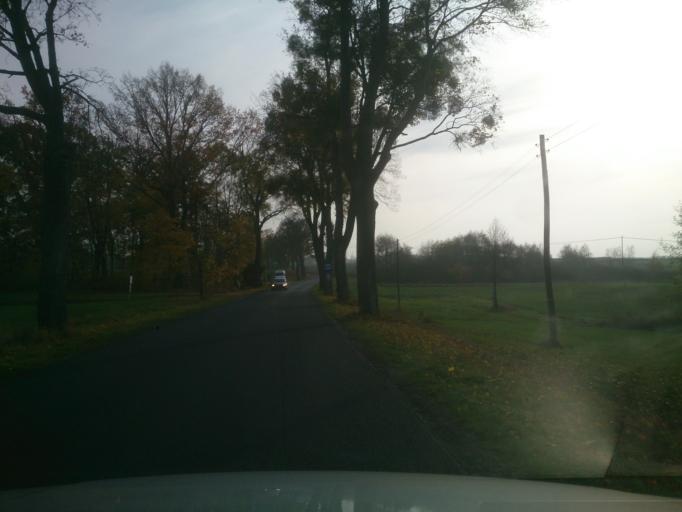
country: PL
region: Kujawsko-Pomorskie
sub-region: Powiat brodnicki
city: Brodnica
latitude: 53.3456
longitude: 19.3749
